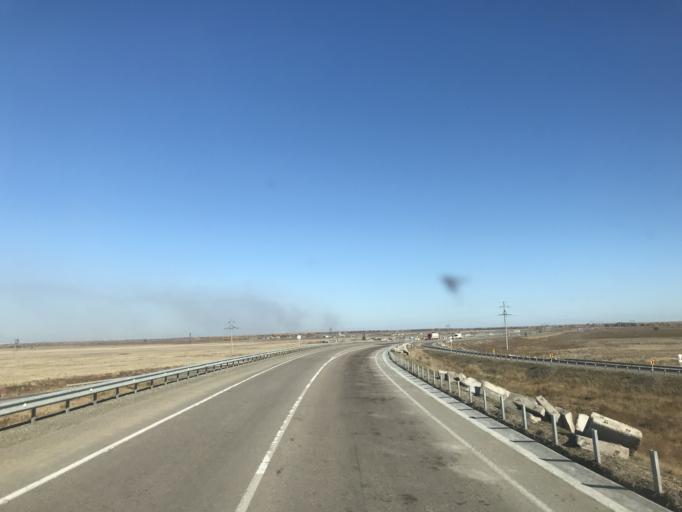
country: KZ
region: Pavlodar
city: Leninskiy
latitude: 52.1544
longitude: 76.8232
